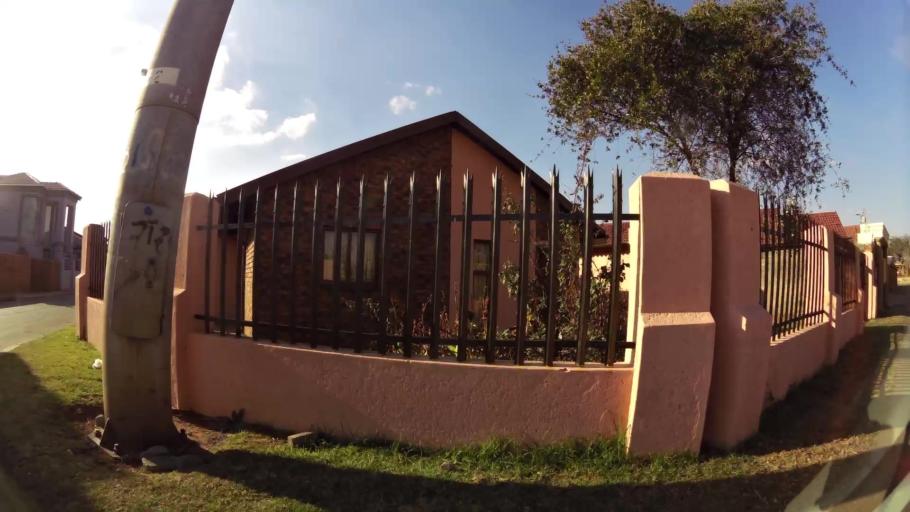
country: ZA
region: Gauteng
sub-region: City of Johannesburg Metropolitan Municipality
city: Soweto
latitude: -26.2683
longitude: 27.9156
